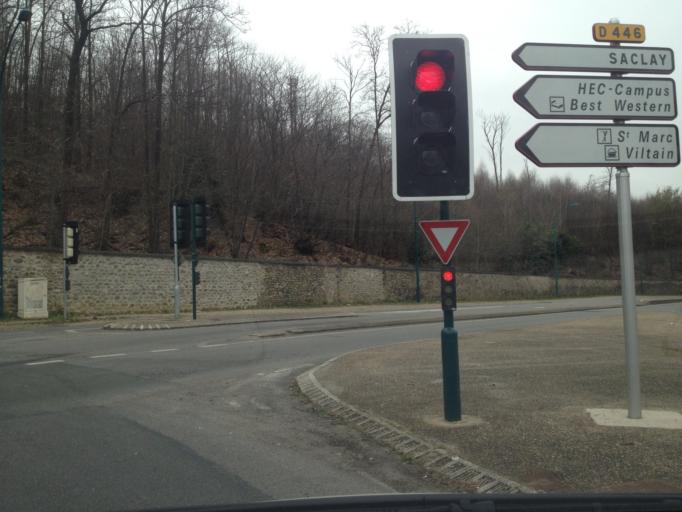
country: FR
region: Ile-de-France
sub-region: Departement des Yvelines
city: Jouy-en-Josas
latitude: 48.7612
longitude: 2.1736
